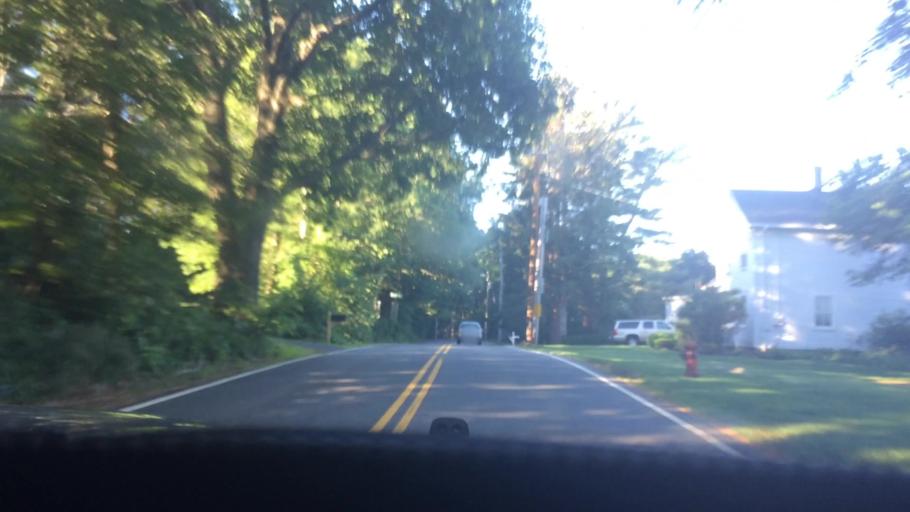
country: US
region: Massachusetts
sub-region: Essex County
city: Andover
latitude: 42.6276
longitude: -71.0931
